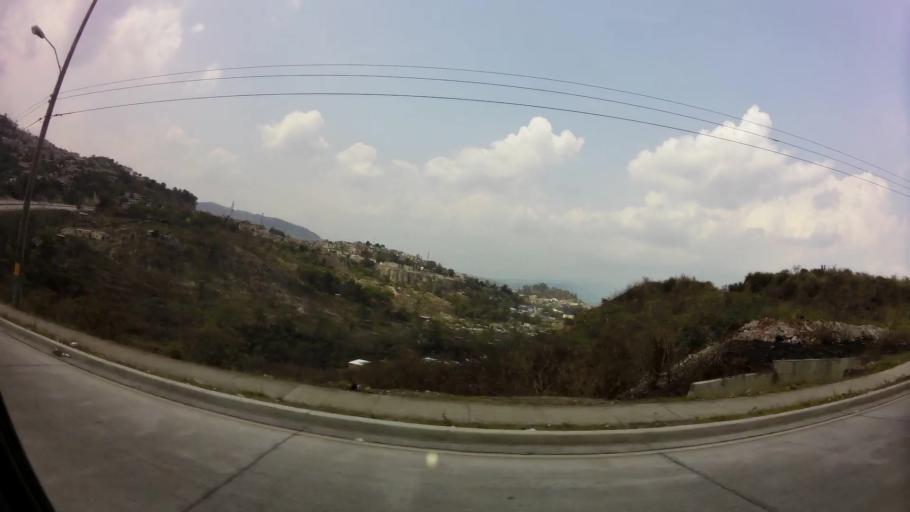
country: HN
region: Francisco Morazan
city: El Lolo
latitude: 14.0851
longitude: -87.2470
